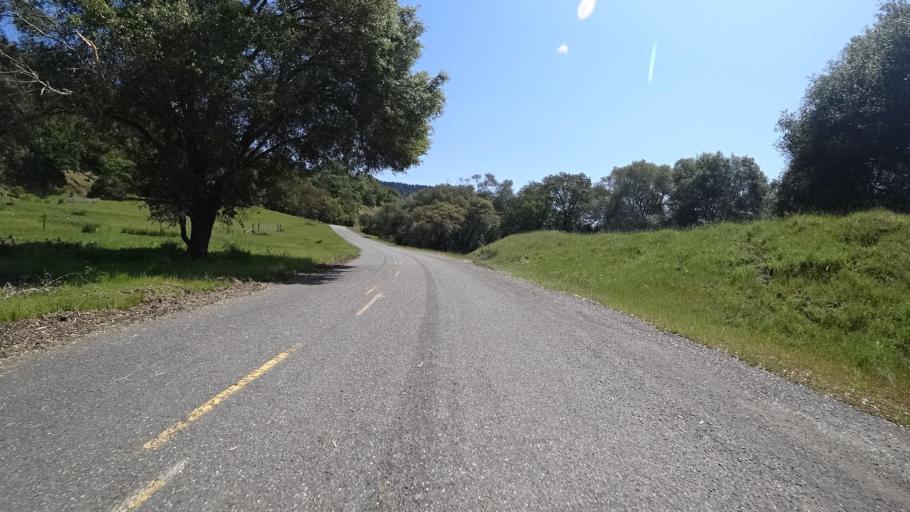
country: US
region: California
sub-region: Humboldt County
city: Redway
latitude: 40.2210
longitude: -123.6343
